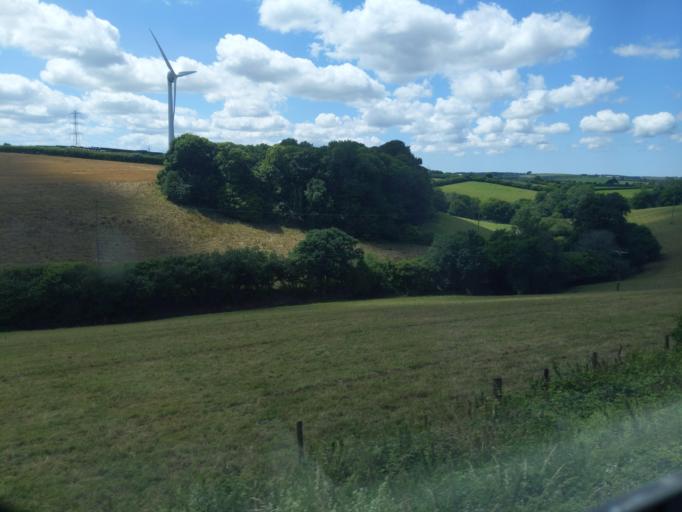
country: GB
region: England
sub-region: Cornwall
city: Liskeard
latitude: 50.4377
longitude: -4.4453
